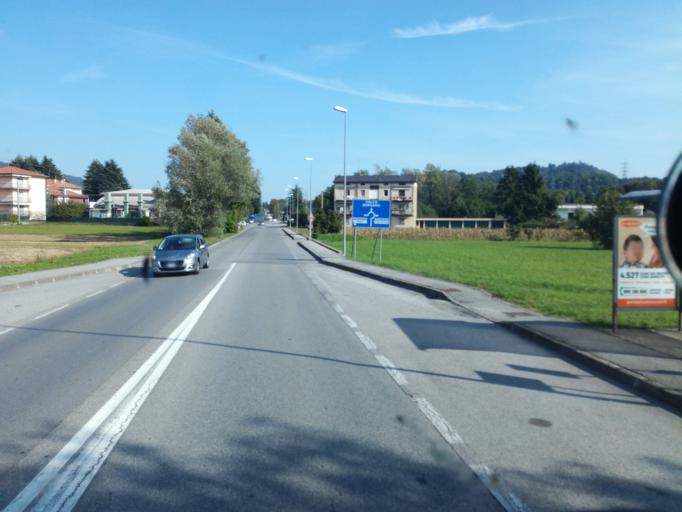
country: IT
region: Lombardy
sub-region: Provincia di Lecco
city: Barzago
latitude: 45.7531
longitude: 9.3168
